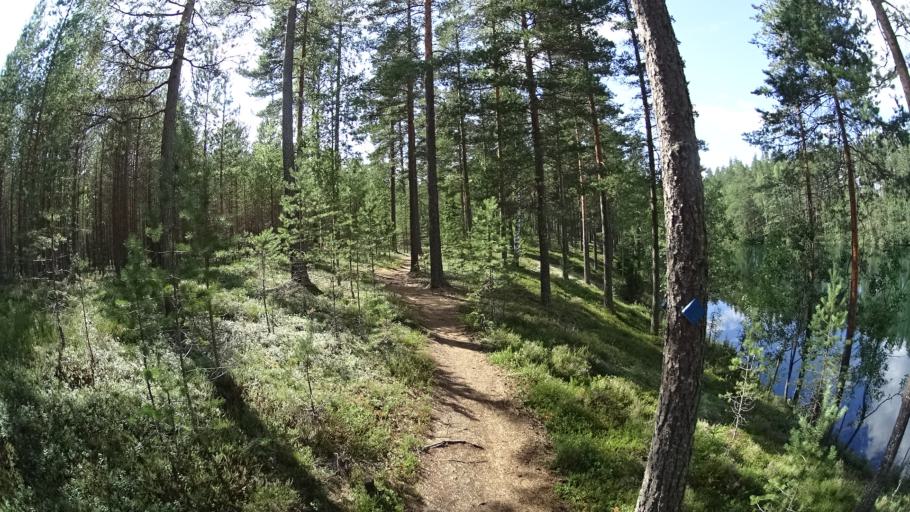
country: FI
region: Uusimaa
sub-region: Helsinki
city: Kaerkoelae
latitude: 60.7341
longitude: 24.0641
